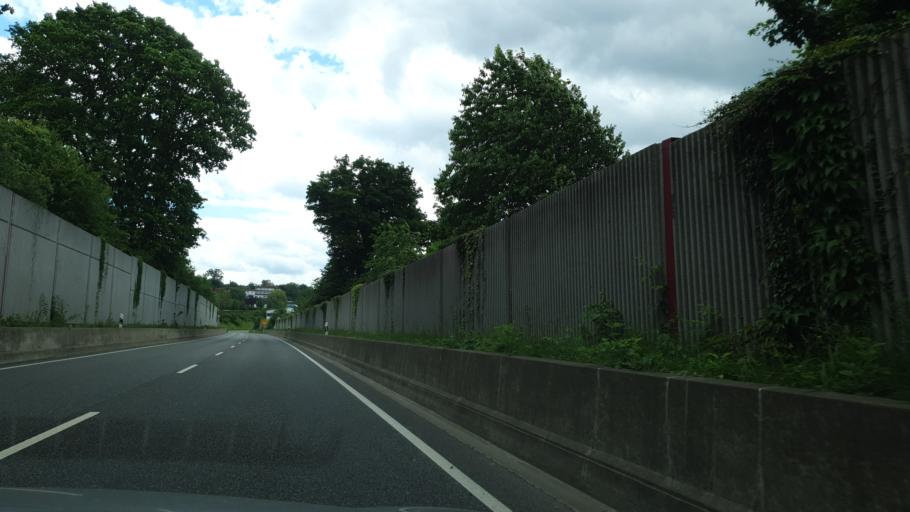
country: DE
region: Rheinland-Pfalz
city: Hohr-Grenzhausen
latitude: 50.4346
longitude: 7.6787
